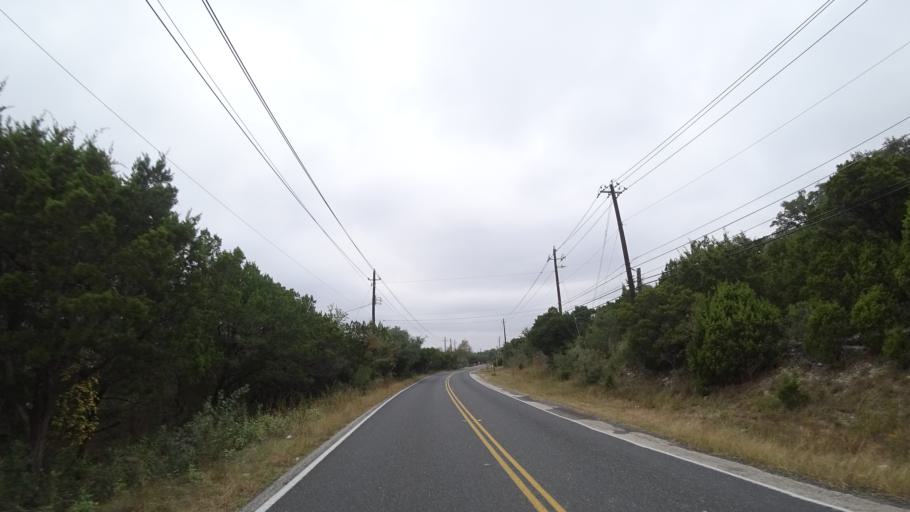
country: US
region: Texas
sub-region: Travis County
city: Barton Creek
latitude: 30.2393
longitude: -97.8757
